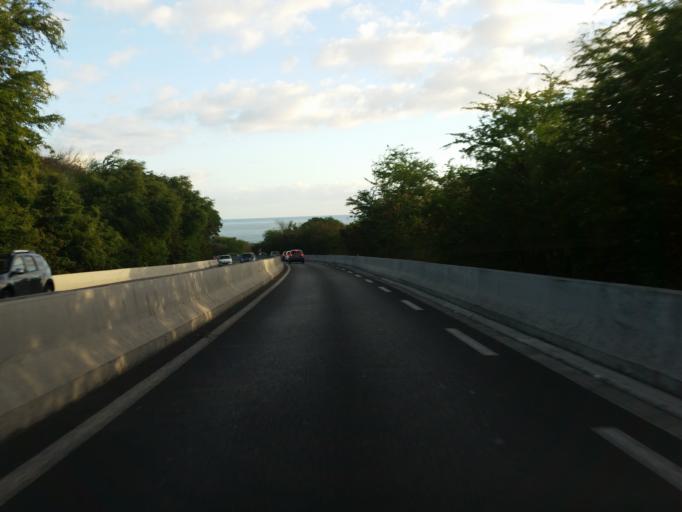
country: RE
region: Reunion
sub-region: Reunion
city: Saint-Denis
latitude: -20.8810
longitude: 55.4388
